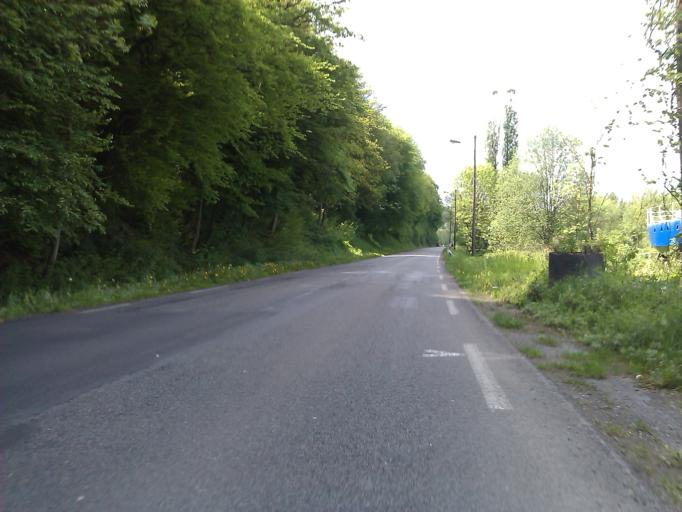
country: FR
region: Franche-Comte
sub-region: Departement du Doubs
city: Courcelles-les-Montbeliard
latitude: 47.5040
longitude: 6.7863
